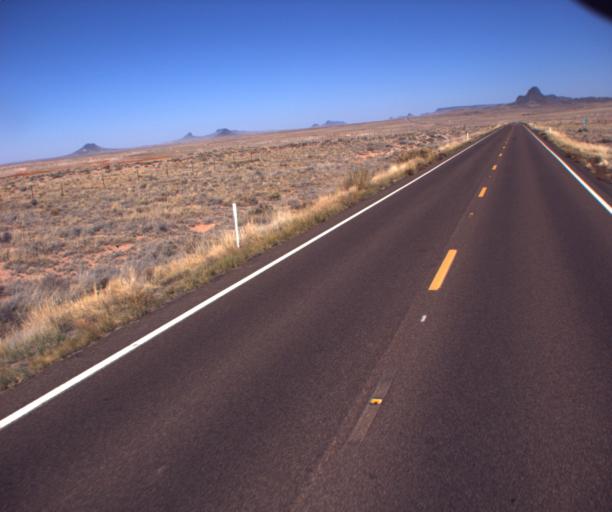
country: US
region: Arizona
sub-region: Navajo County
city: Dilkon
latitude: 35.2295
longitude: -110.4330
